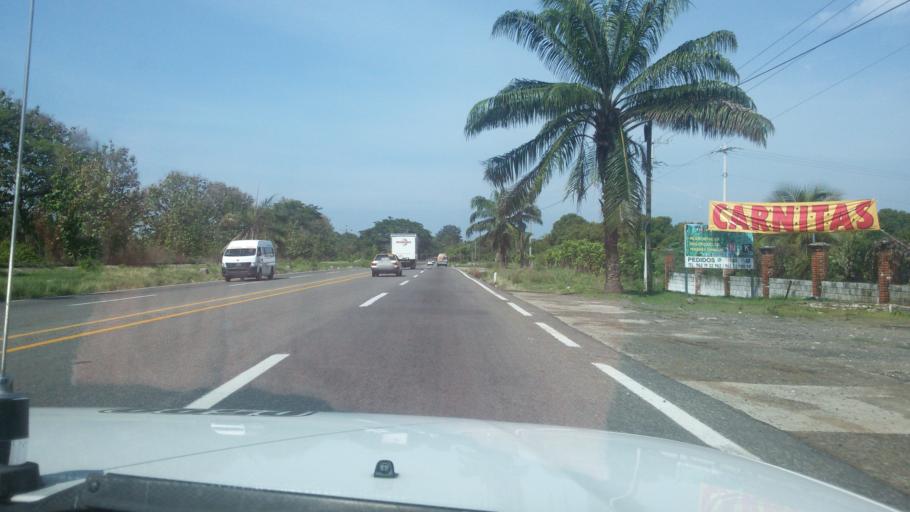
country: MX
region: Chiapas
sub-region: Tapachula
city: Vida Mejor I
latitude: 14.8278
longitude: -92.3315
